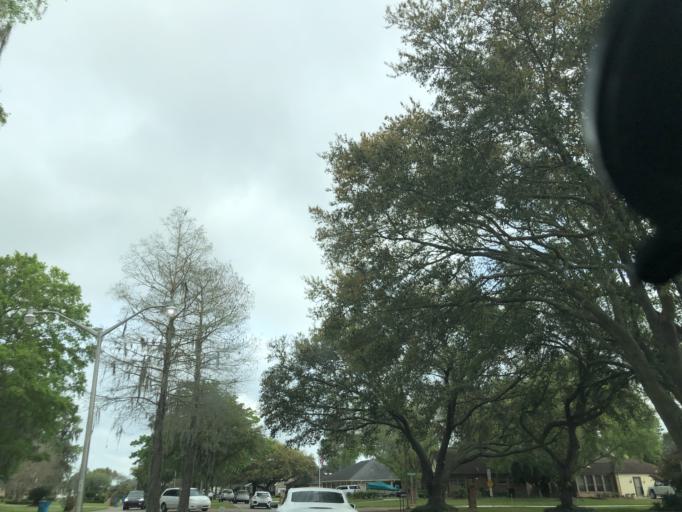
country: US
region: Louisiana
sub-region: Saint Charles Parish
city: New Sarpy
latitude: 29.9797
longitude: -90.3630
